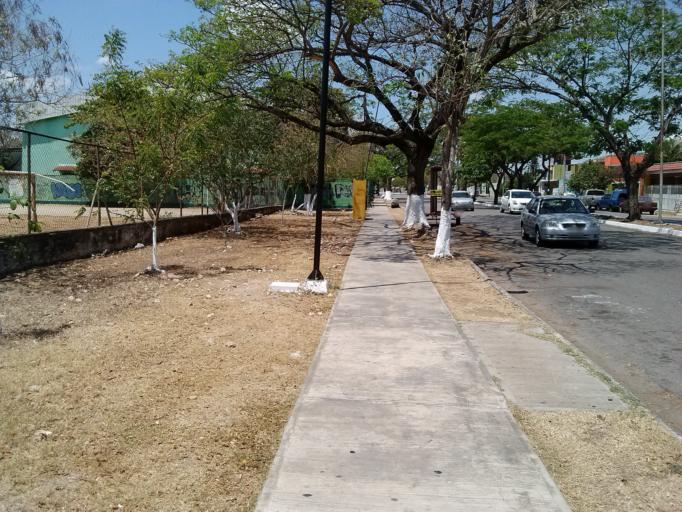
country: MX
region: Yucatan
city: Merida
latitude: 20.9698
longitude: -89.5863
